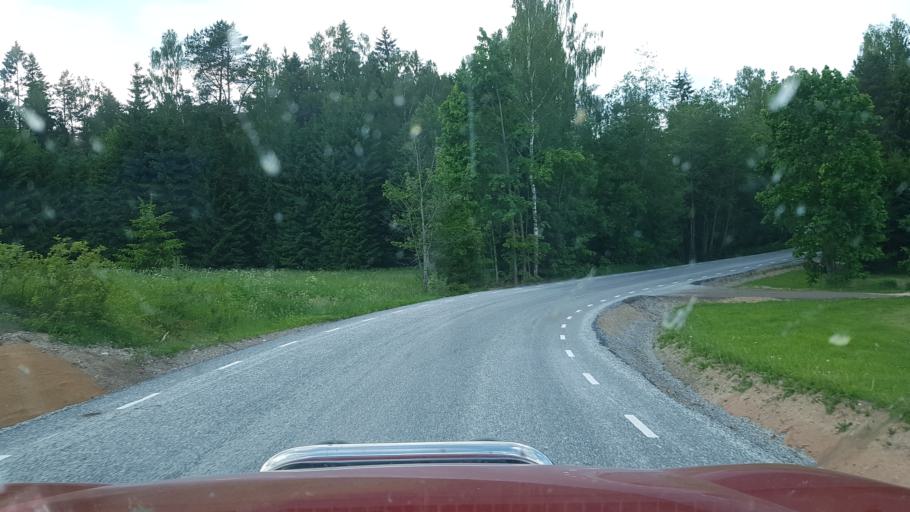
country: EE
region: Tartu
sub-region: UElenurme vald
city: Ulenurme
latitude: 58.0923
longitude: 26.8076
